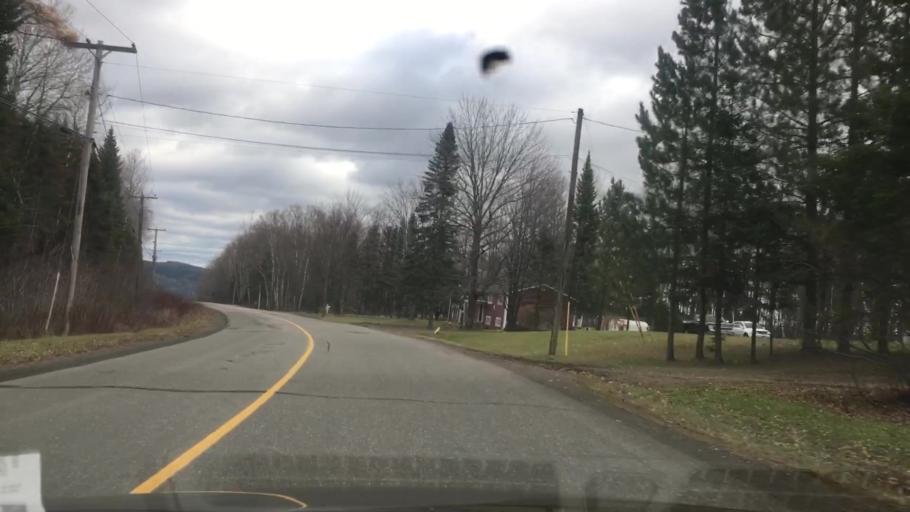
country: US
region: Maine
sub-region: Aroostook County
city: Fort Fairfield
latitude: 46.7477
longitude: -67.7466
